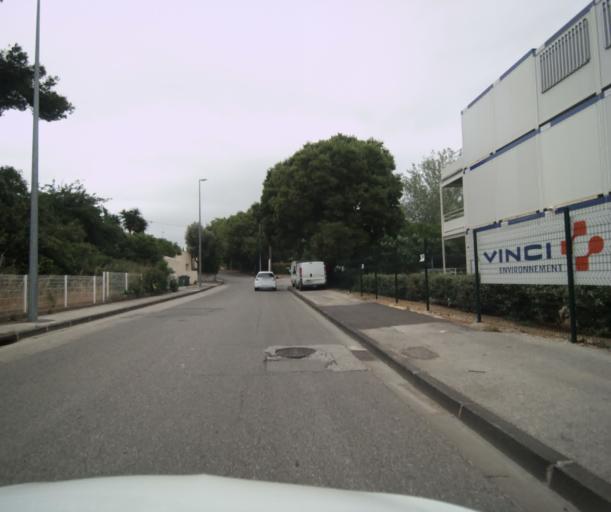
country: FR
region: Provence-Alpes-Cote d'Azur
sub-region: Departement du Var
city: La Seyne-sur-Mer
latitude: 43.1255
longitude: 5.8897
